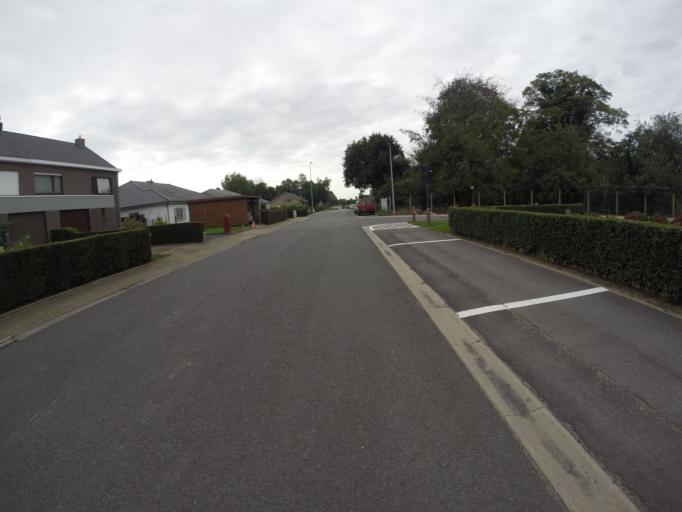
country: BE
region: Flanders
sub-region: Provincie West-Vlaanderen
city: Ruiselede
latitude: 51.0393
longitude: 3.3974
